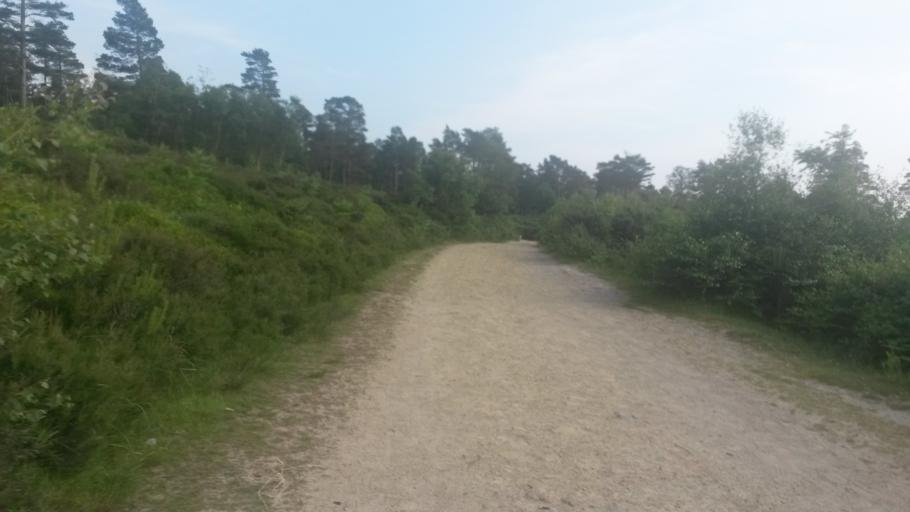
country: GB
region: England
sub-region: West Sussex
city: Fernhurst
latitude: 51.0578
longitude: -0.6911
